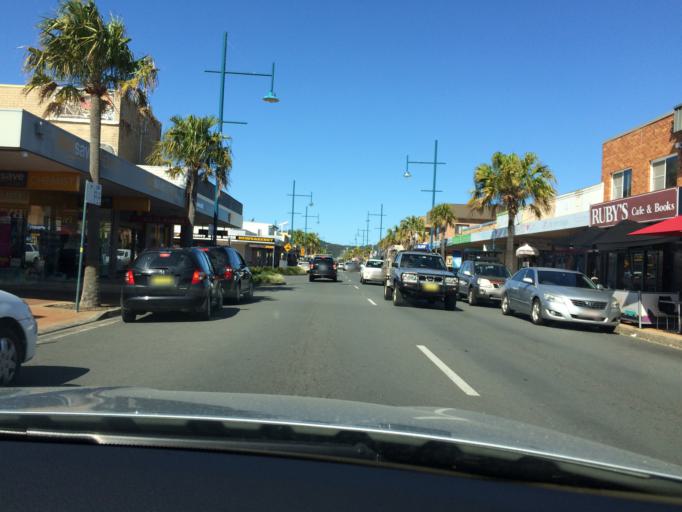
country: AU
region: New South Wales
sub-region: Gosford Shire
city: Umina
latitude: -33.5213
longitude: 151.3182
